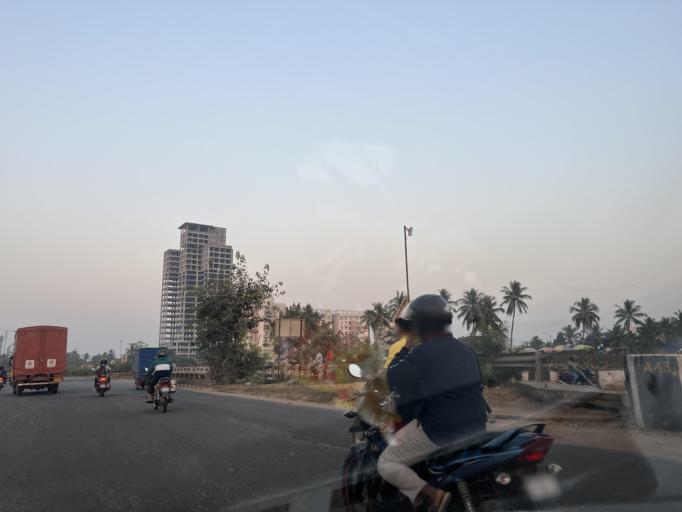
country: IN
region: Odisha
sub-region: Khordha
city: Bhubaneshwar
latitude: 20.3192
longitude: 85.8807
